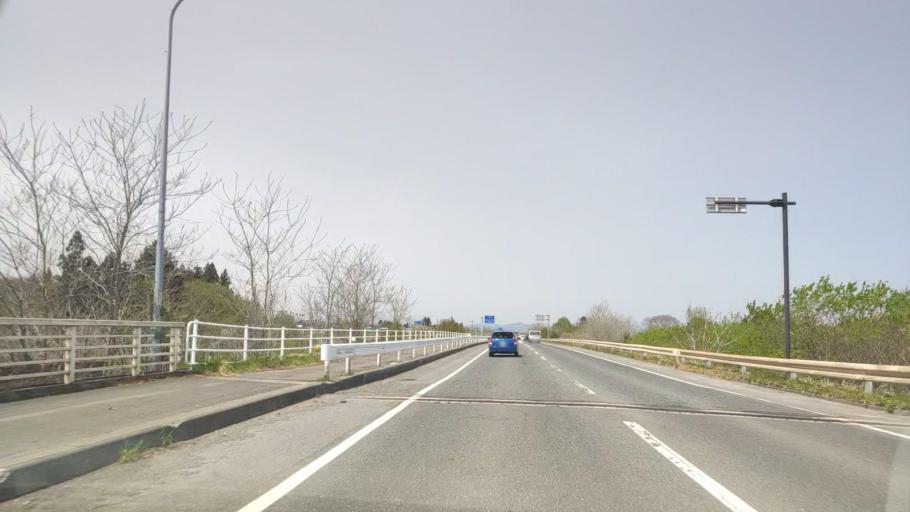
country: JP
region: Aomori
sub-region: Misawa Shi
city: Inuotose
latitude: 40.6314
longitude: 141.2478
